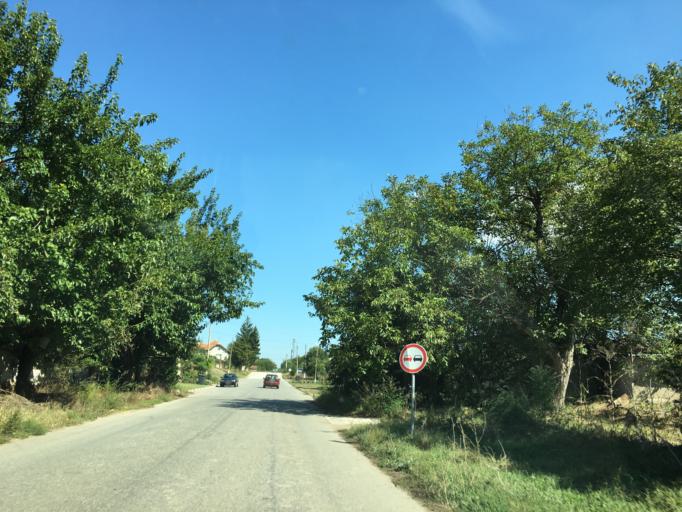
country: RO
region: Olt
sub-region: Comuna Orlea
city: Orlea
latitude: 43.6353
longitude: 24.3943
